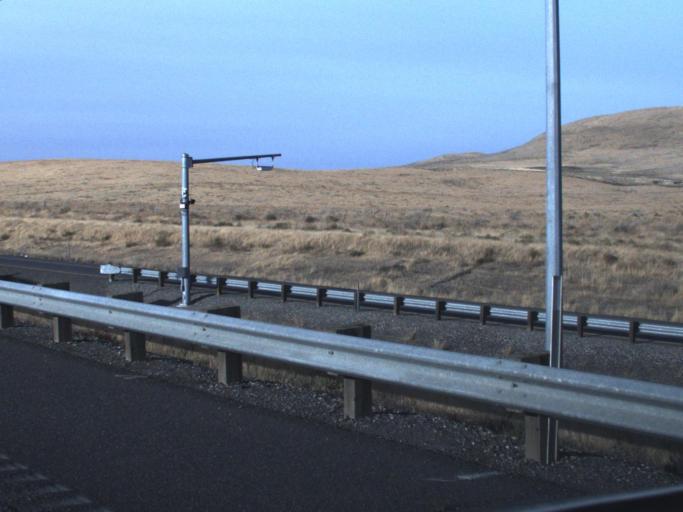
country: US
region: Oregon
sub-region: Umatilla County
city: Umatilla
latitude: 45.9472
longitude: -119.3358
